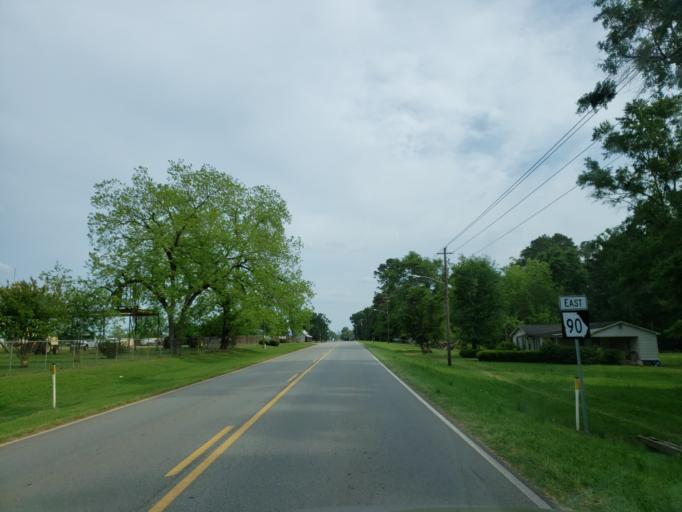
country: US
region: Georgia
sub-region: Dooly County
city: Vienna
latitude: 32.1449
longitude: -83.8767
